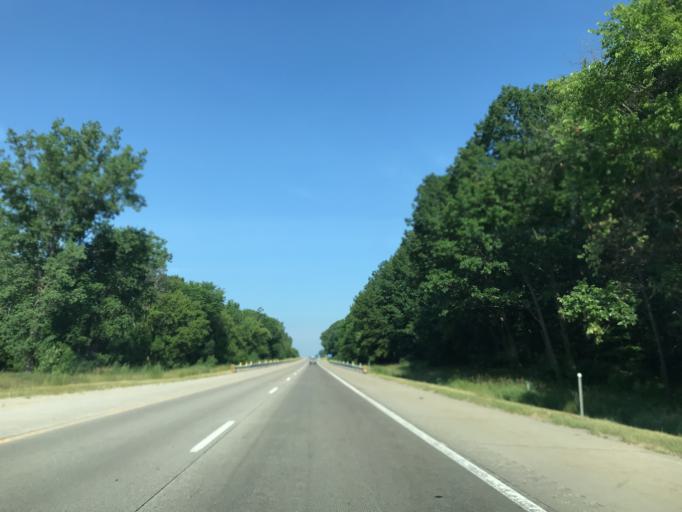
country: US
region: Michigan
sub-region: Ingham County
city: Okemos
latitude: 42.6760
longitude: -84.3936
